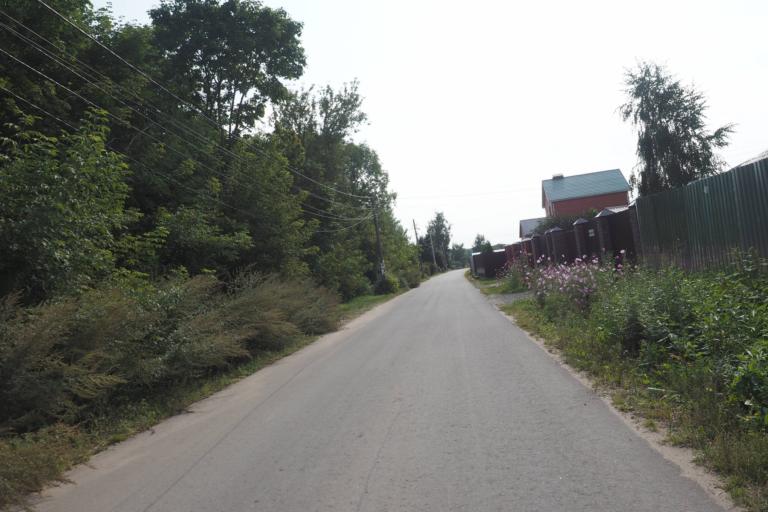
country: RU
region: Moskovskaya
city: Ramenskoye
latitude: 55.5516
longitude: 38.2895
